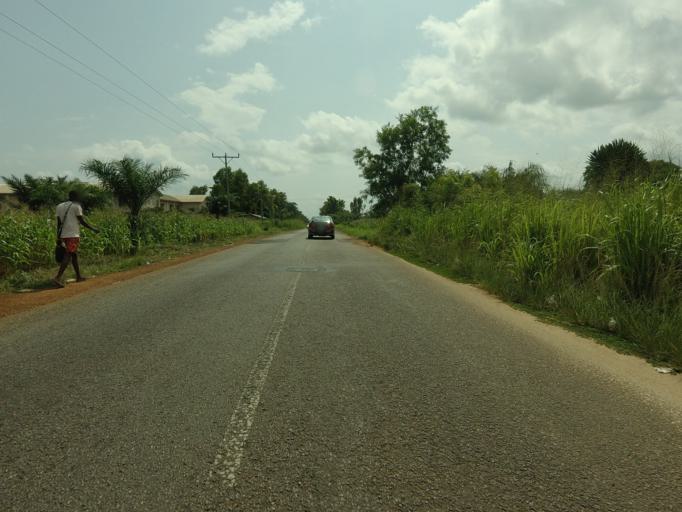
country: TG
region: Maritime
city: Lome
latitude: 6.2270
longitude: 1.0194
